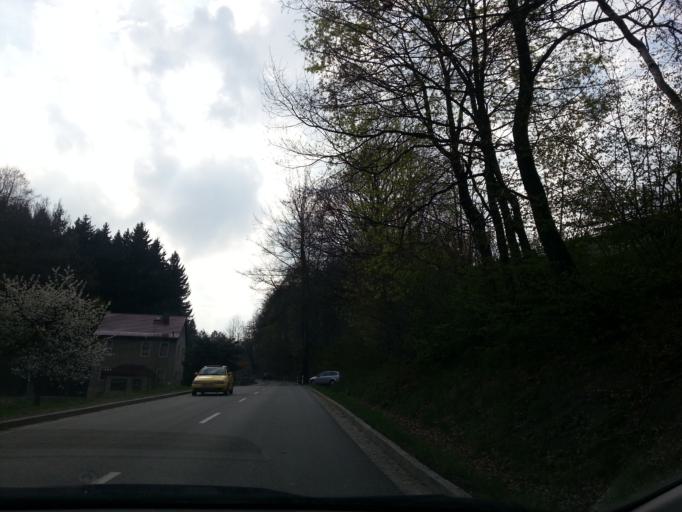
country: DE
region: Saxony
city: Schmiedeberg
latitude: 50.8487
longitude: 13.6653
